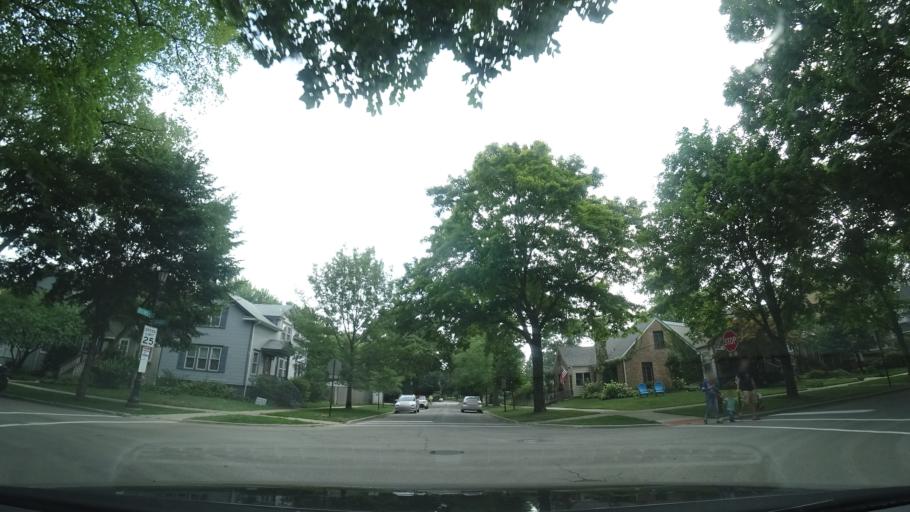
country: US
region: Illinois
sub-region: Cook County
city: Evanston
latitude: 42.0594
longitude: -87.7004
